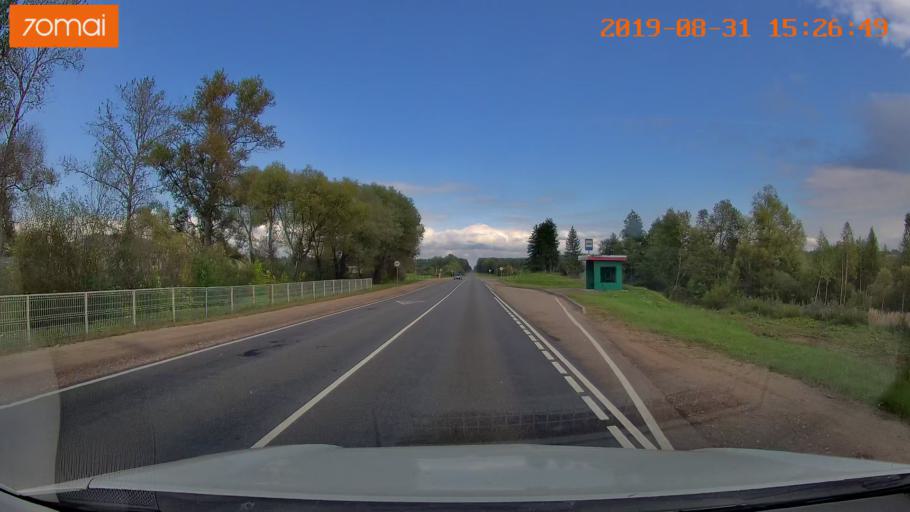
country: RU
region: Kaluga
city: Baryatino
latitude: 54.5523
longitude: 34.5457
